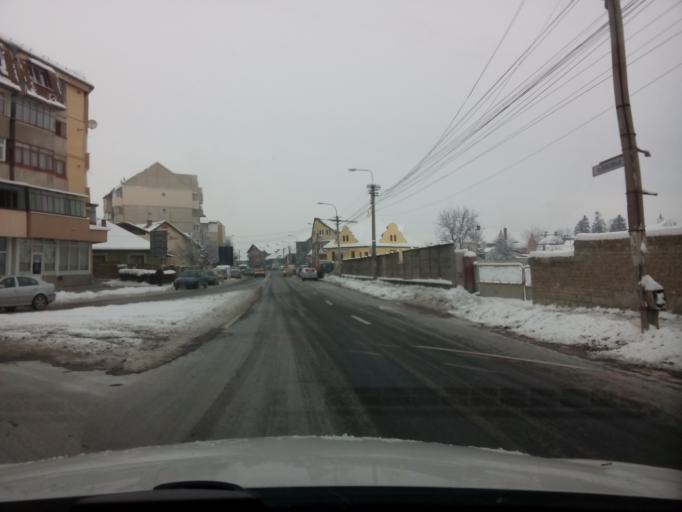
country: RO
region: Sibiu
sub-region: Municipiul Sibiu
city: Sibiu
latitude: 45.8053
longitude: 24.1519
